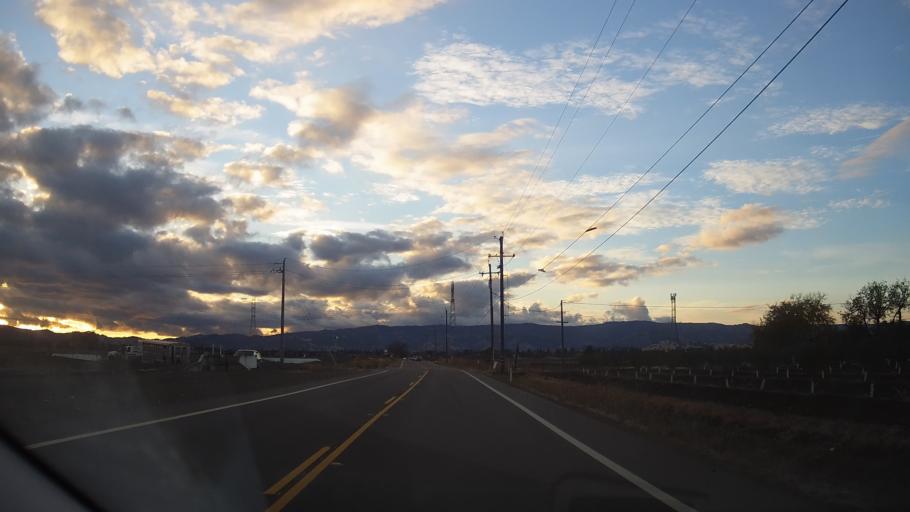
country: US
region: California
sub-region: Solano County
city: Hartley
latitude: 38.3590
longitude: -121.9146
